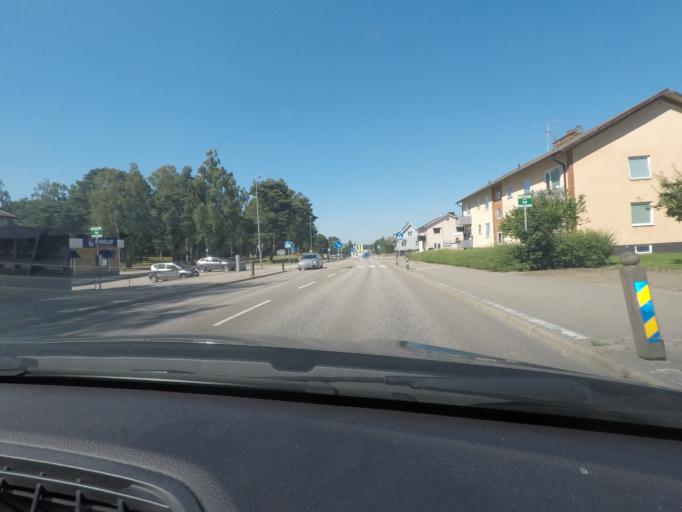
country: SE
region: Kronoberg
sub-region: Markaryds Kommun
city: Markaryd
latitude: 56.4530
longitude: 13.5957
